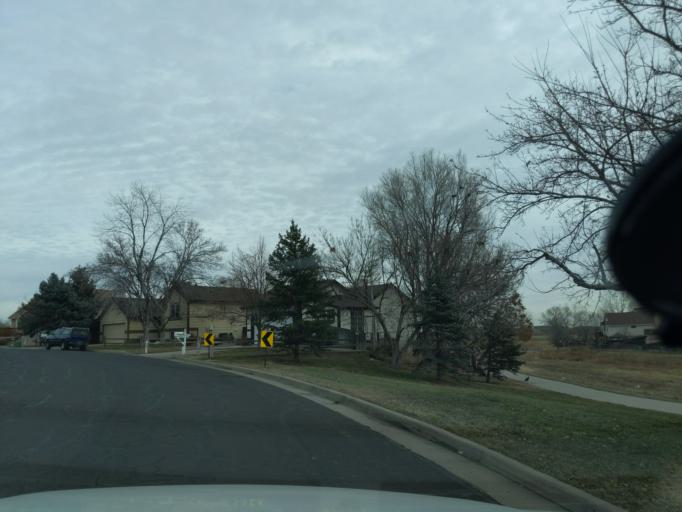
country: US
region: Colorado
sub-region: Adams County
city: Thornton
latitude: 39.8689
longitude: -104.9522
